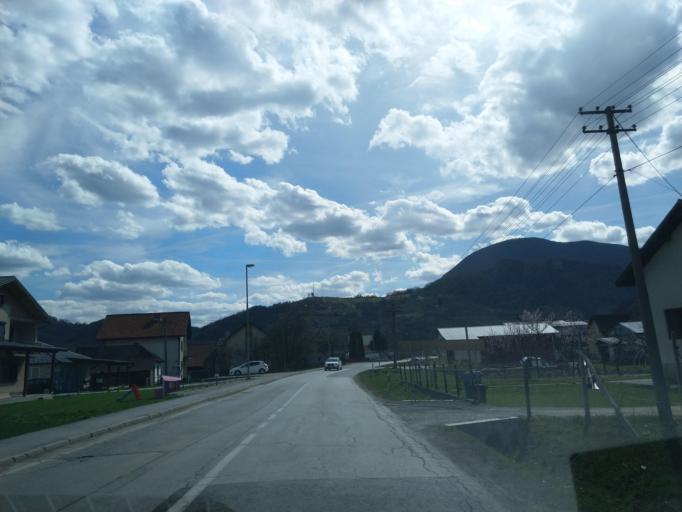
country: RS
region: Central Serbia
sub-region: Zlatiborski Okrug
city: Arilje
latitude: 43.6779
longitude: 20.1259
